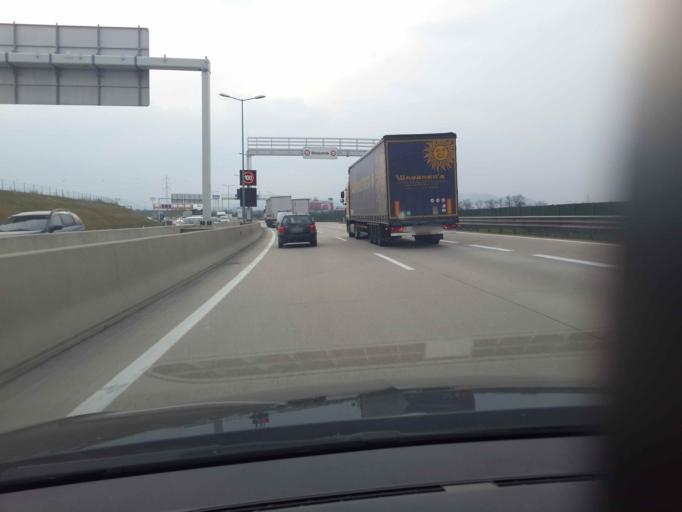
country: AT
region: Lower Austria
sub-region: Politischer Bezirk Modling
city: Vosendorf
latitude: 48.1320
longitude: 16.3375
